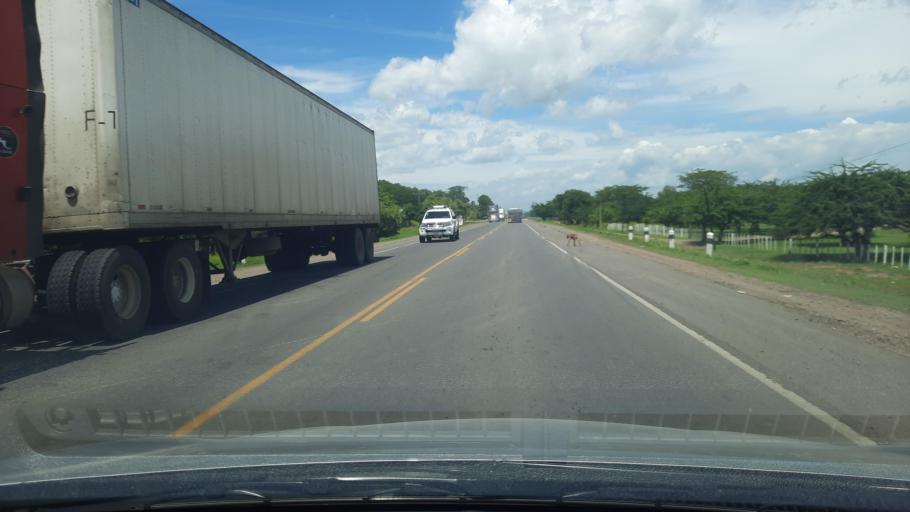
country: NI
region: Chinandega
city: Somotillo
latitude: 13.0585
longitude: -86.9273
